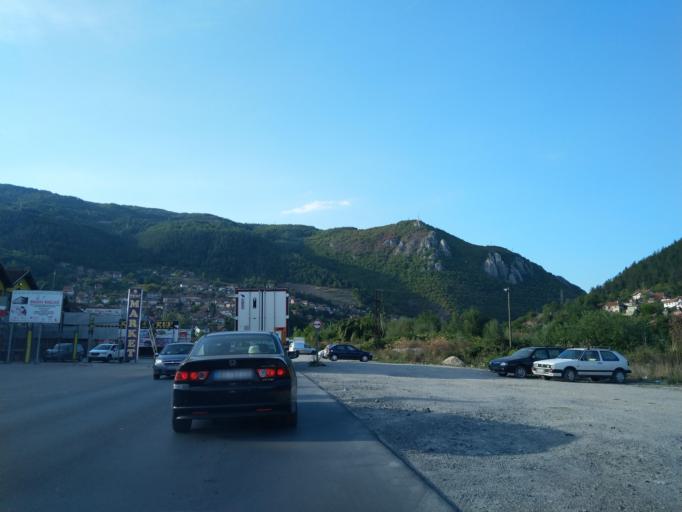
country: RS
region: Central Serbia
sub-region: Zlatiborski Okrug
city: Prijepolje
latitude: 43.3700
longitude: 19.6324
